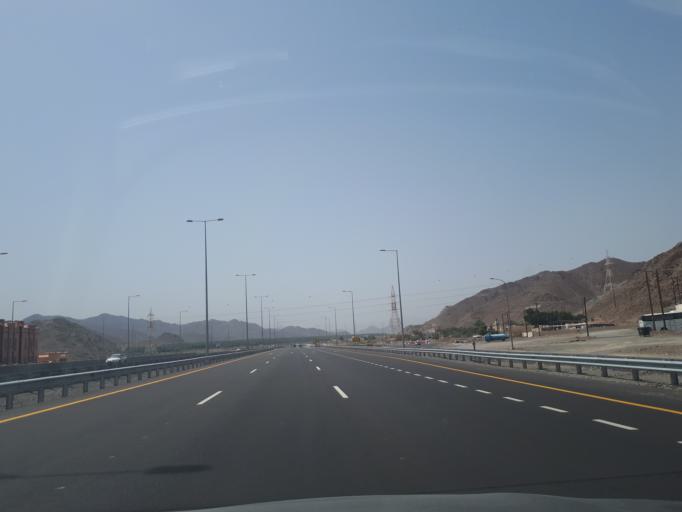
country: OM
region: Muhafazat ad Dakhiliyah
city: Bidbid
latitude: 23.3878
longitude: 58.1013
